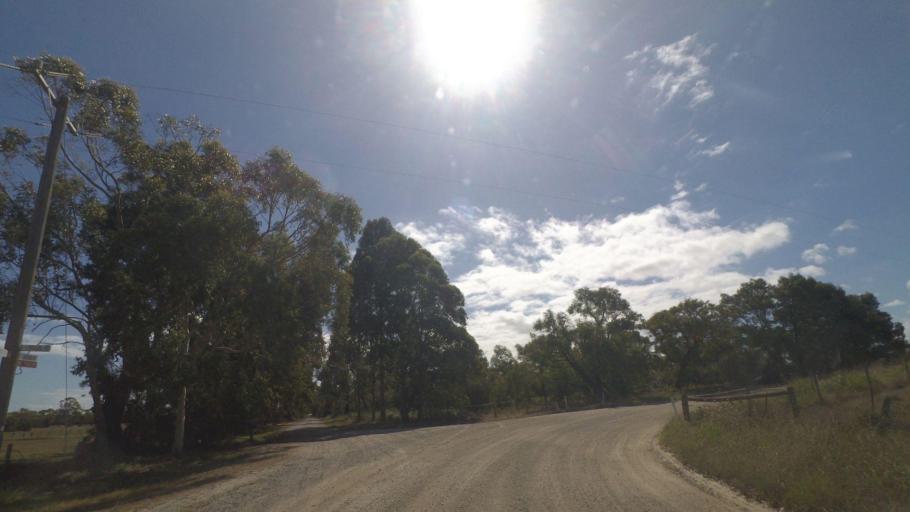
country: AU
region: Victoria
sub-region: Cardinia
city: Garfield
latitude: -38.2617
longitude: 145.6571
